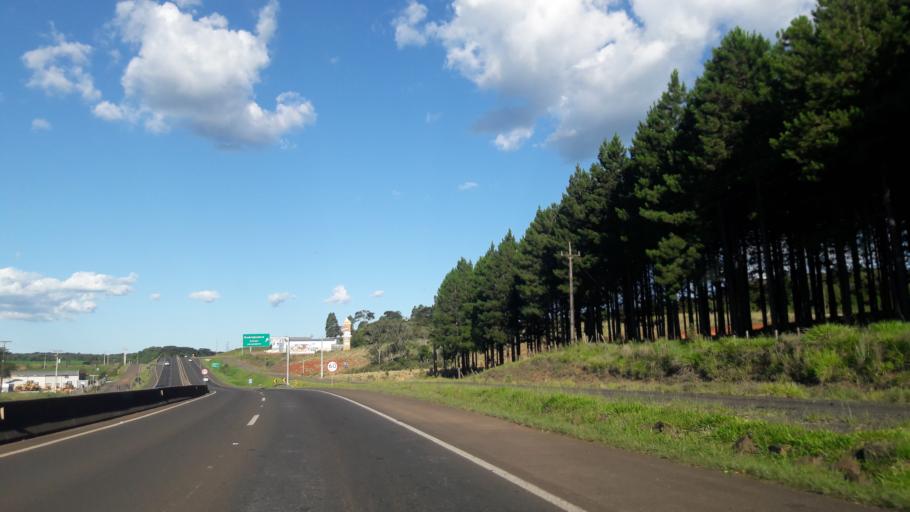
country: BR
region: Parana
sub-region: Guarapuava
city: Guarapuava
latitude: -25.3429
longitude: -51.4356
